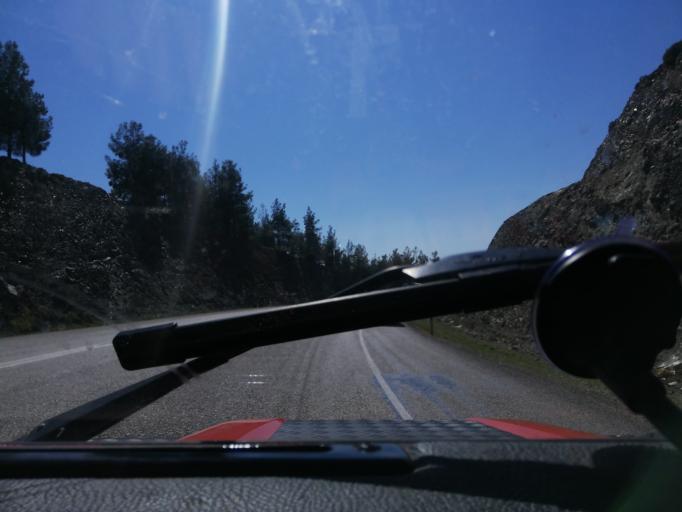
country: TR
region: Mugla
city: Kemer
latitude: 36.6093
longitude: 29.3586
